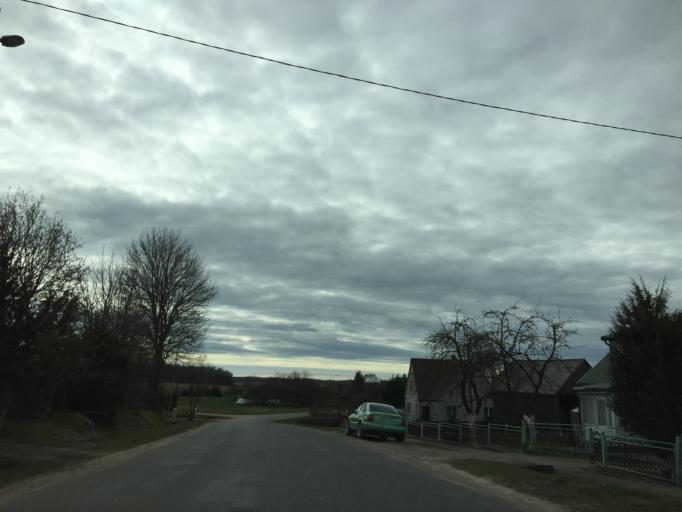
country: LT
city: Silale
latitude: 55.6208
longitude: 22.2267
